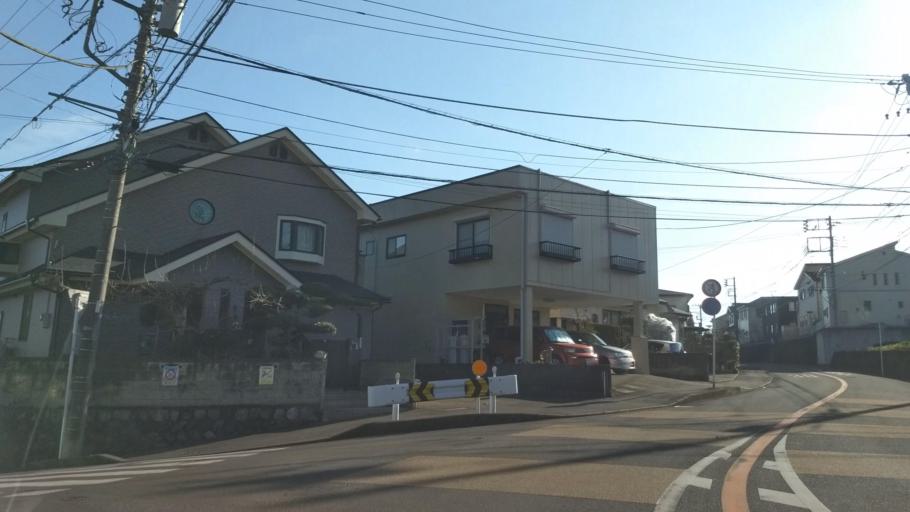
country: JP
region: Kanagawa
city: Hadano
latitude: 35.3640
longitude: 139.2526
